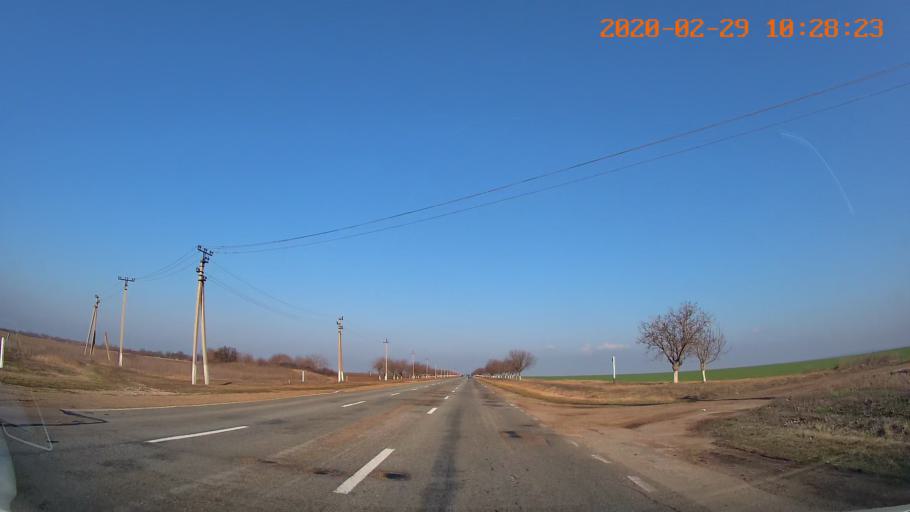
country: MD
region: Telenesti
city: Tiraspolul Nou
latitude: 46.9098
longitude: 29.5917
